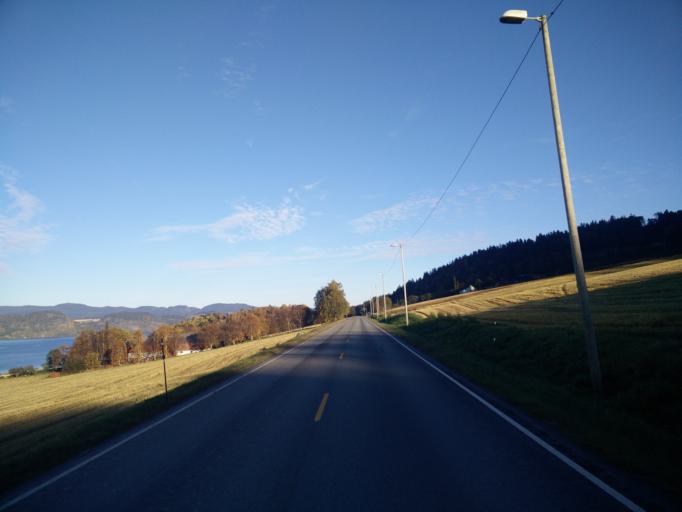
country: NO
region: Sor-Trondelag
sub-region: Skaun
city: Borsa
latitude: 63.3462
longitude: 10.0189
